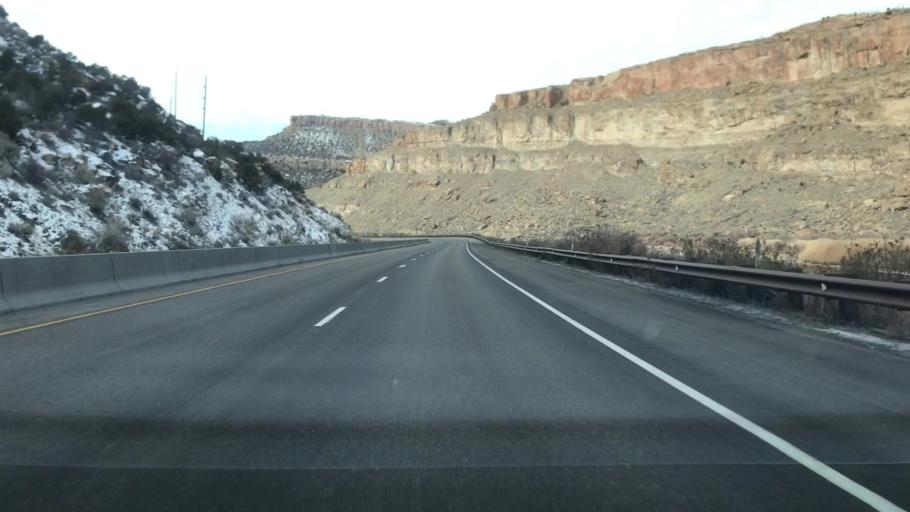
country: US
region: Colorado
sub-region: Mesa County
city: Palisade
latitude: 39.2383
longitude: -108.2620
